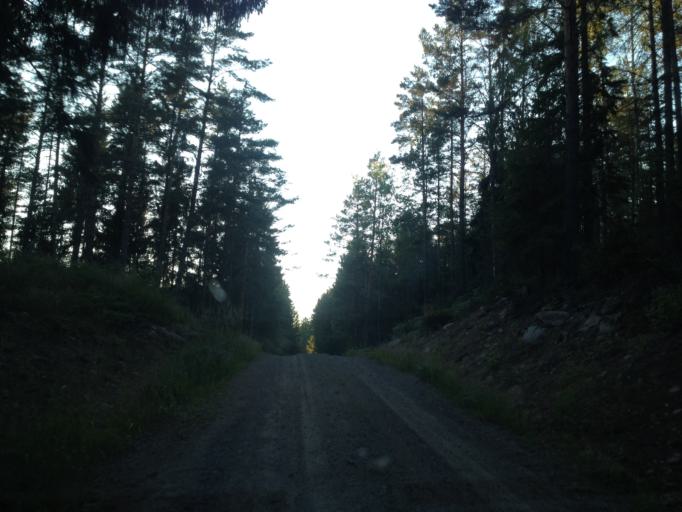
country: SE
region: Kalmar
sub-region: Vasterviks Kommun
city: Overum
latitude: 57.9978
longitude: 16.1356
